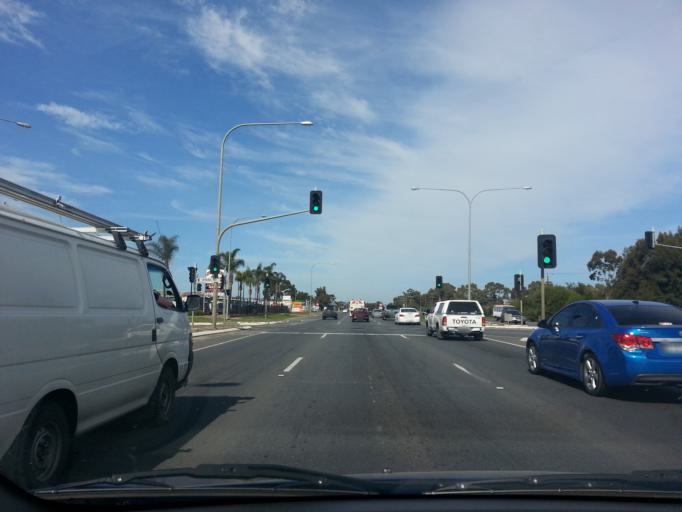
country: AU
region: South Australia
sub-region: Salisbury
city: Salisbury
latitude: -34.7879
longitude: 138.5963
